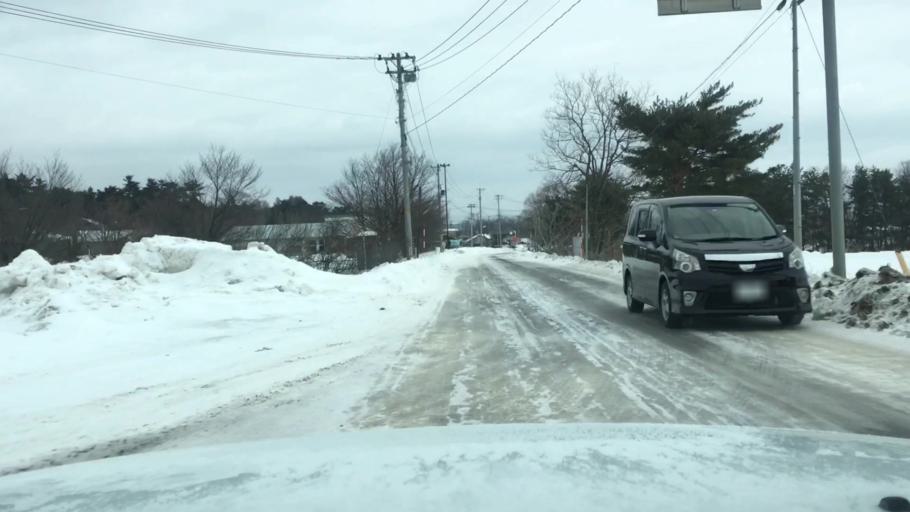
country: JP
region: Iwate
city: Shizukuishi
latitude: 39.9136
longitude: 141.0052
